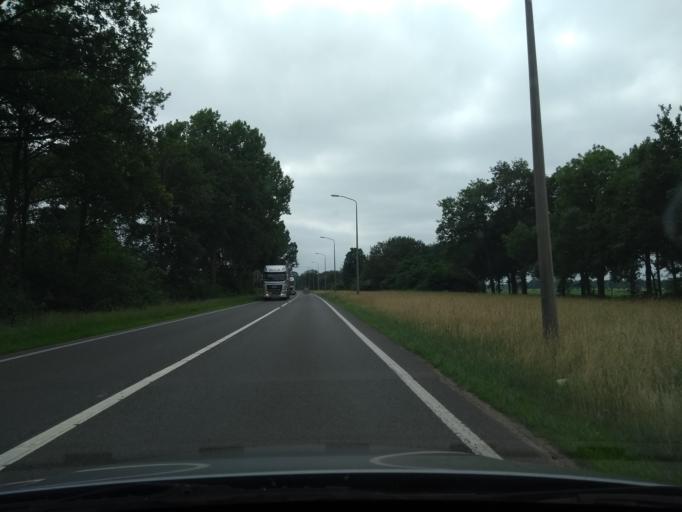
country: NL
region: Overijssel
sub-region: Gemeente Wierden
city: Wierden
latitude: 52.3492
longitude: 6.6246
